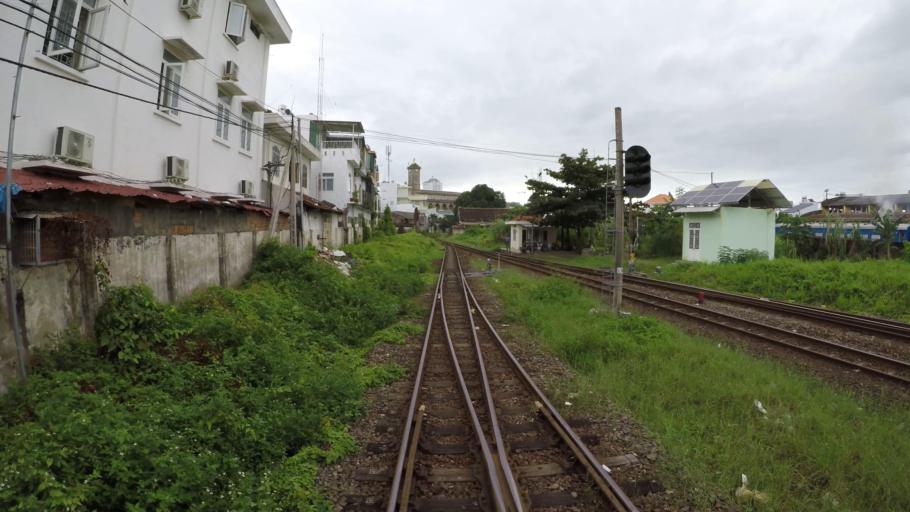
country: VN
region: Khanh Hoa
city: Nha Trang
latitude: 12.2456
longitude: 109.1881
